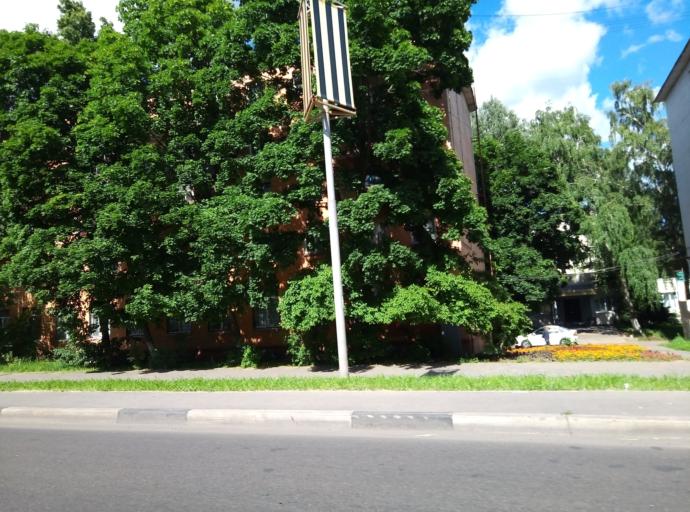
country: RU
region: Kursk
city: Kursk
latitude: 51.7601
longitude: 36.1867
